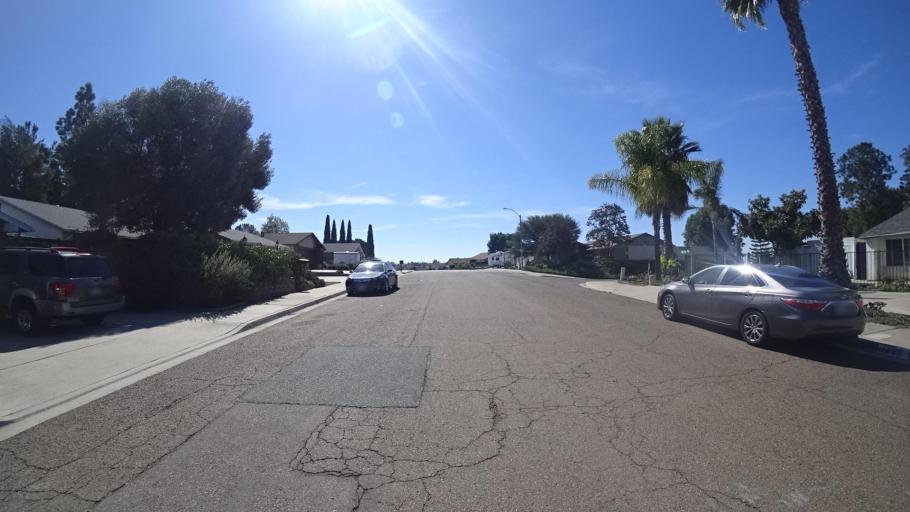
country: US
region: California
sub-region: San Diego County
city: Casa de Oro-Mount Helix
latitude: 32.7522
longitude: -116.9725
